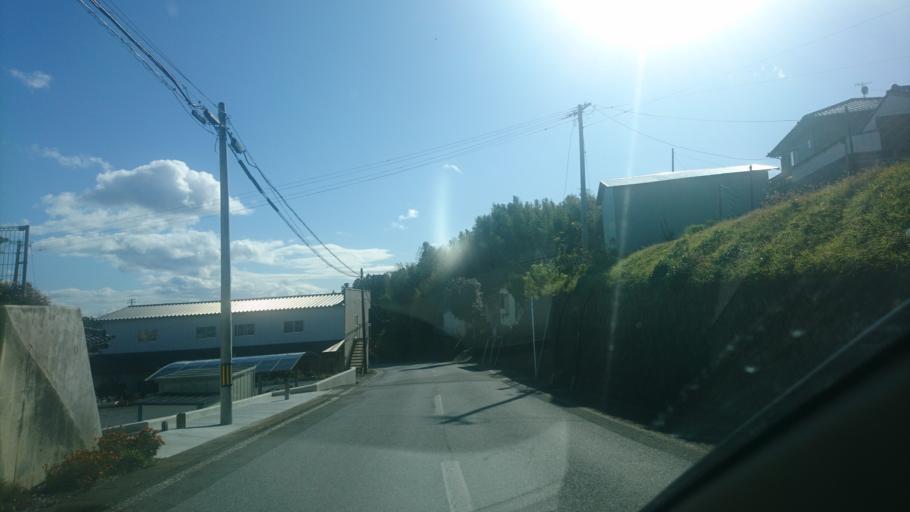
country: JP
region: Iwate
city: Ofunato
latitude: 38.9903
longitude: 141.7344
